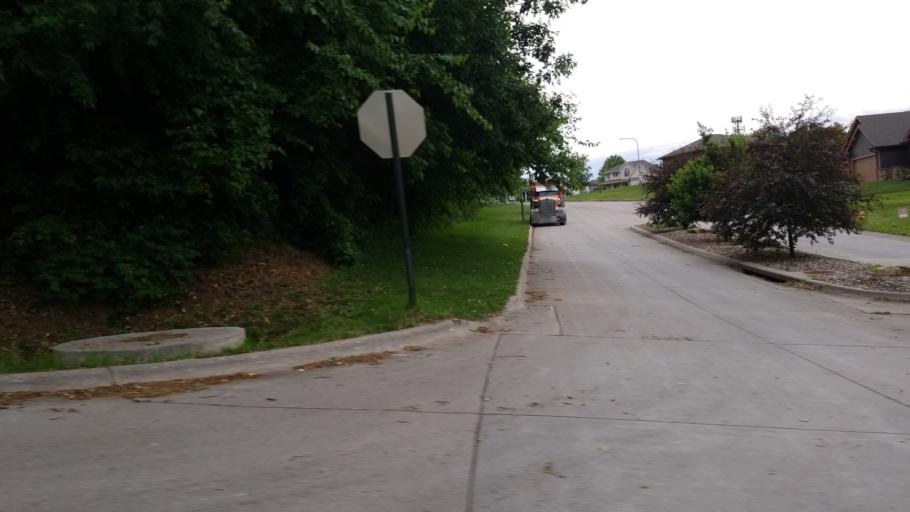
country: US
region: Nebraska
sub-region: Sarpy County
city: Offutt Air Force Base
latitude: 41.1710
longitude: -95.9335
